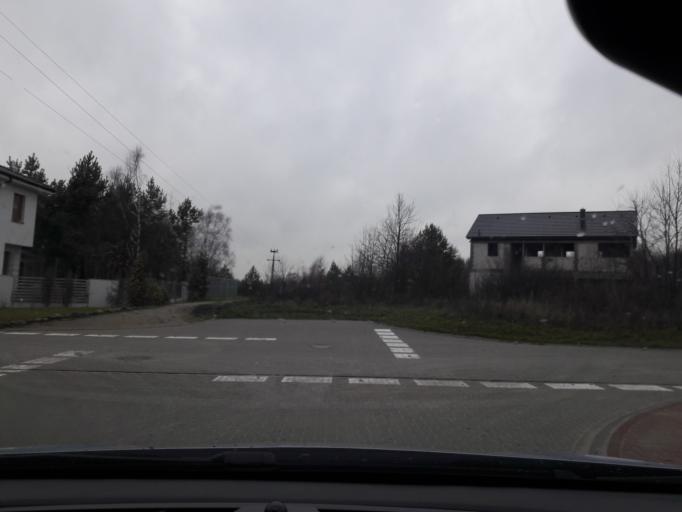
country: PL
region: Greater Poland Voivodeship
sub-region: Powiat poznanski
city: Suchy Las
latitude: 52.4860
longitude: 16.8837
